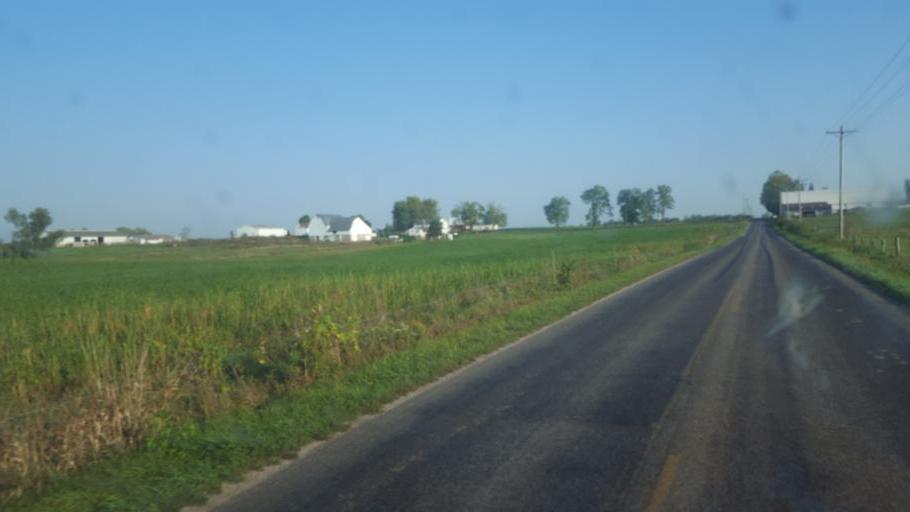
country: US
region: Indiana
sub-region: LaGrange County
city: Lagrange
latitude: 41.5950
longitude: -85.4241
